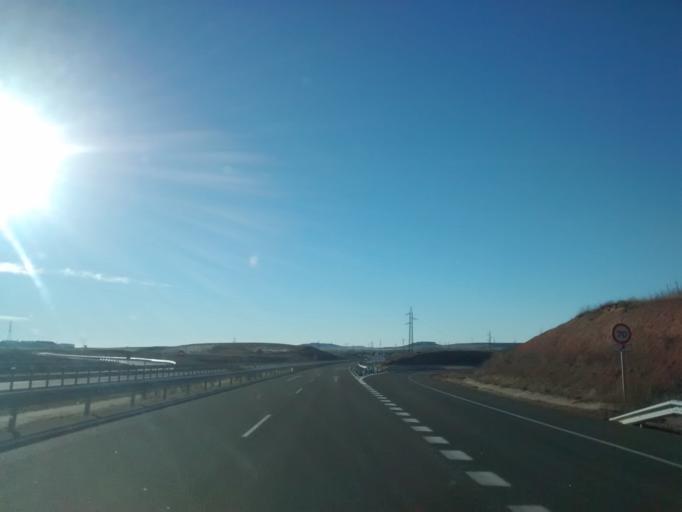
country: ES
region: Castille and Leon
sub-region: Provincia de Palencia
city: Herrera de Pisuerga
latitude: 42.6152
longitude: -4.3494
